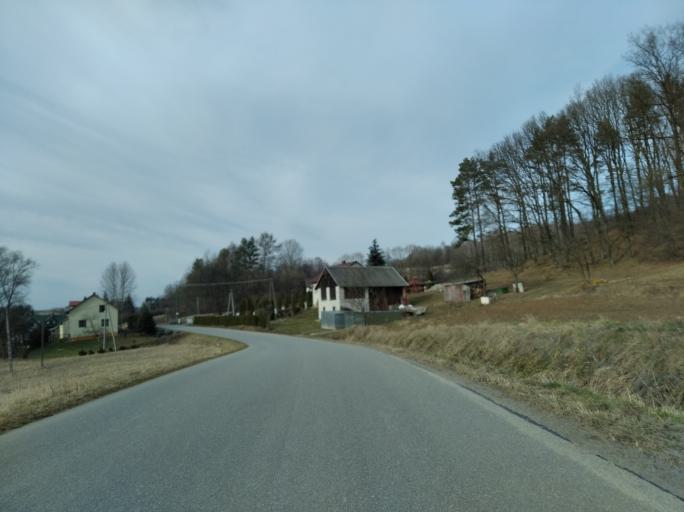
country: PL
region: Subcarpathian Voivodeship
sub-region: Powiat brzozowski
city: Gorki
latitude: 49.6393
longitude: 22.0561
